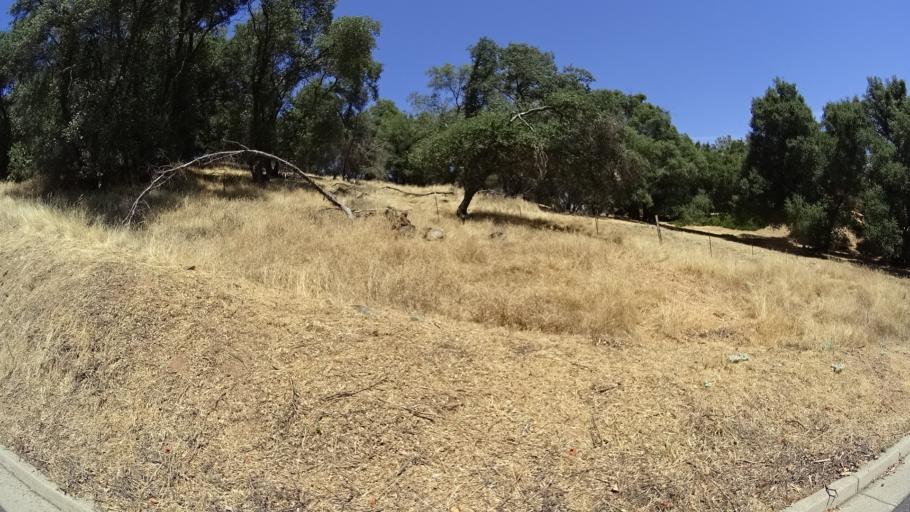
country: US
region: California
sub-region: Calaveras County
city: Angels Camp
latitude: 38.0691
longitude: -120.5514
